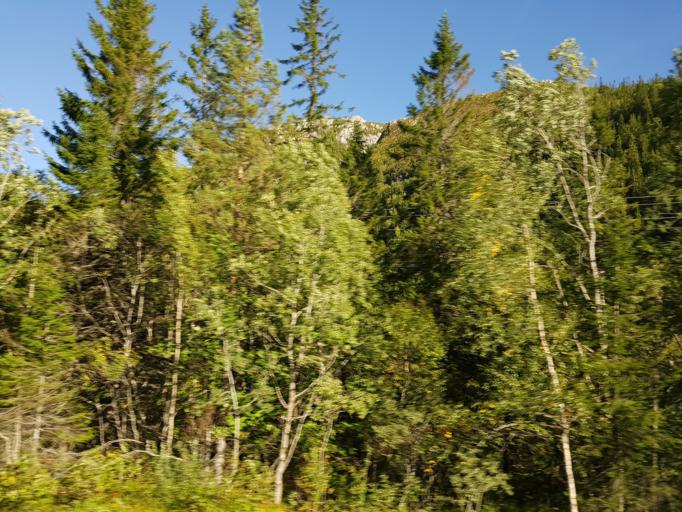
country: NO
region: Sor-Trondelag
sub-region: Afjord
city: A i Afjord
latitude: 63.7163
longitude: 10.2350
